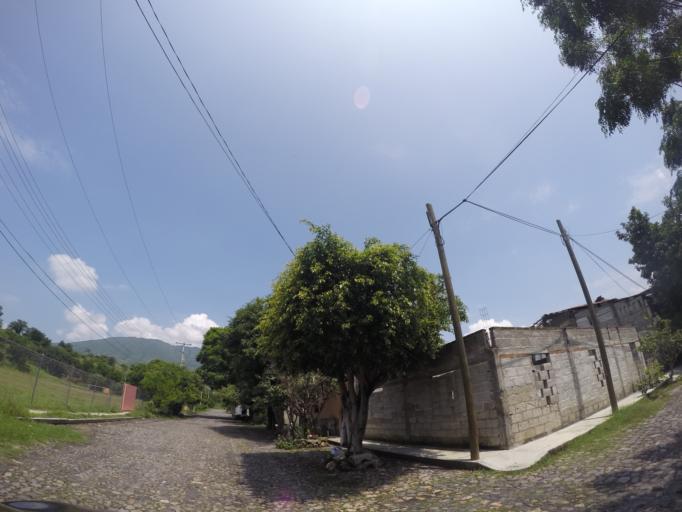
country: MX
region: Nayarit
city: Jala
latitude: 21.1074
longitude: -104.4339
